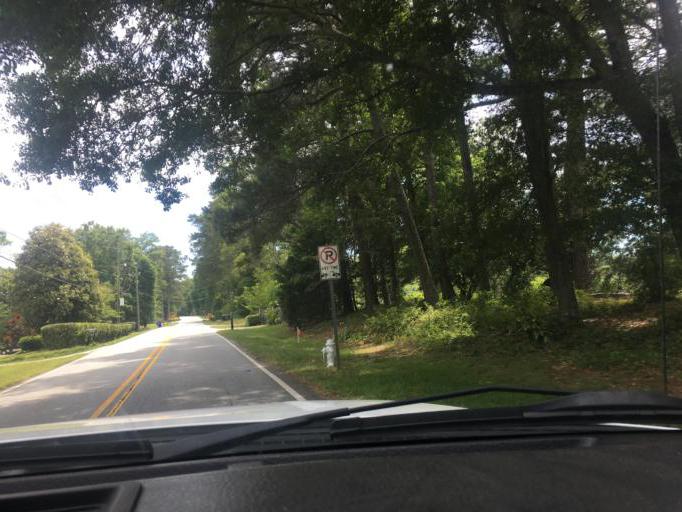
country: US
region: Georgia
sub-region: Rockdale County
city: Lakeview Estates
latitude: 33.7158
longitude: -84.0588
